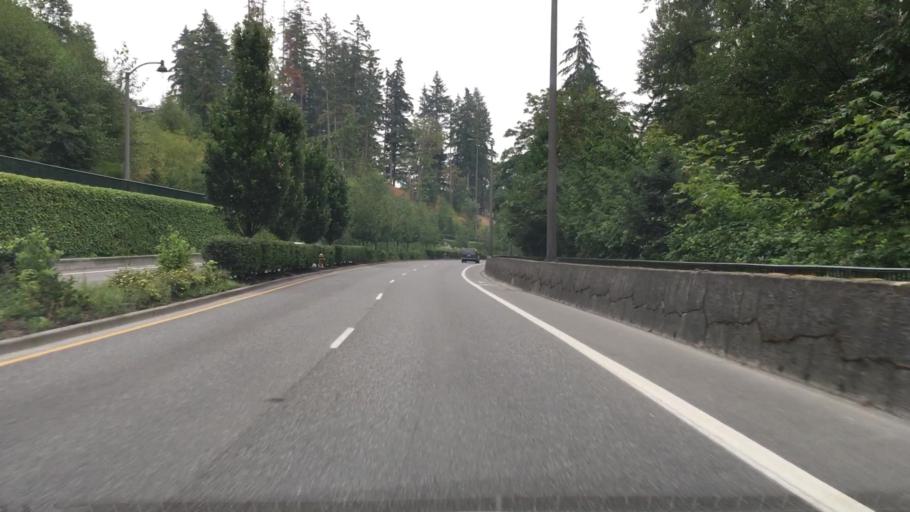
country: US
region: Washington
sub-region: King County
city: Newcastle
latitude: 47.5234
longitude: -122.1614
